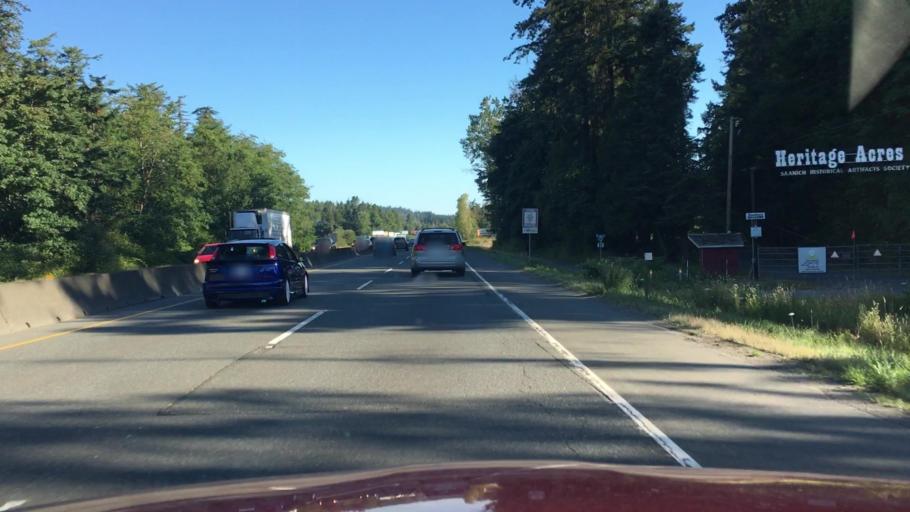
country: CA
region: British Columbia
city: North Saanich
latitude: 48.5793
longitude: -123.3989
